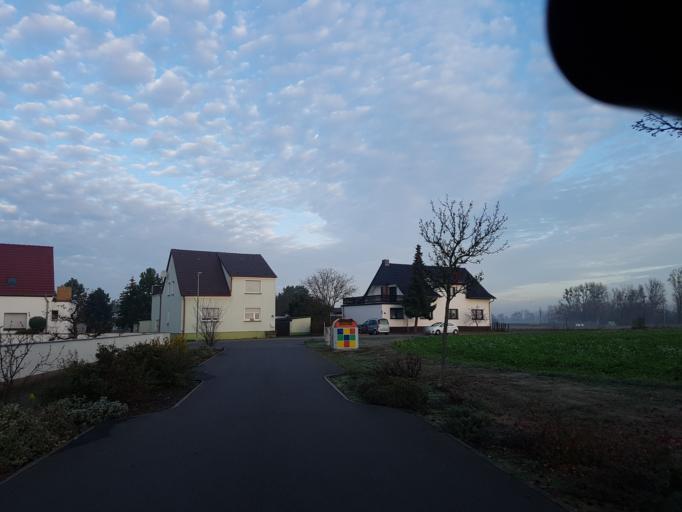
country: DE
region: Saxony-Anhalt
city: Elster
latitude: 51.8212
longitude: 12.8546
